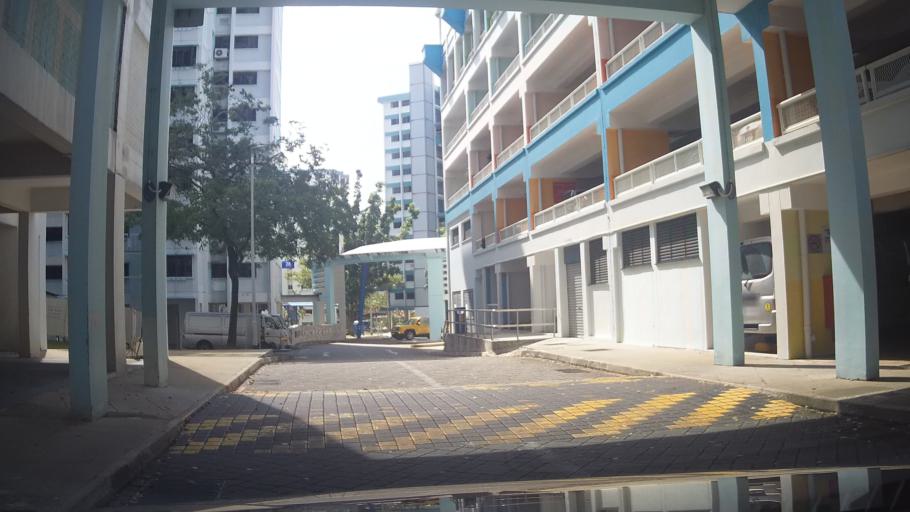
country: MY
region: Johor
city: Johor Bahru
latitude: 1.4429
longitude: 103.7737
